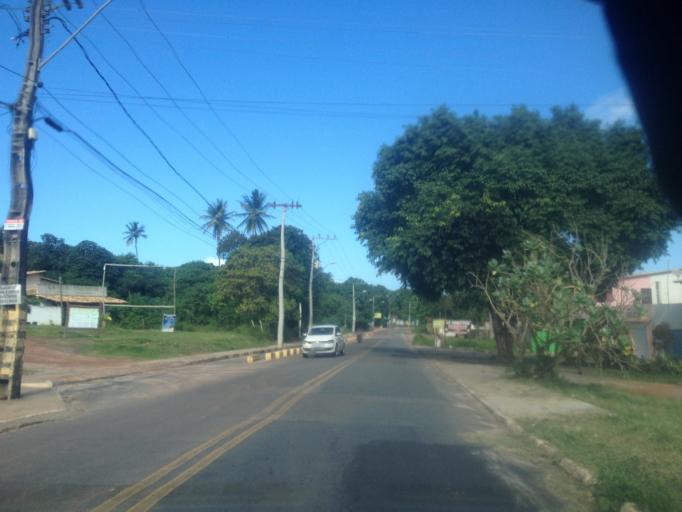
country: BR
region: Bahia
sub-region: Mata De Sao Joao
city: Mata de Sao Joao
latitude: -12.5961
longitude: -38.0424
